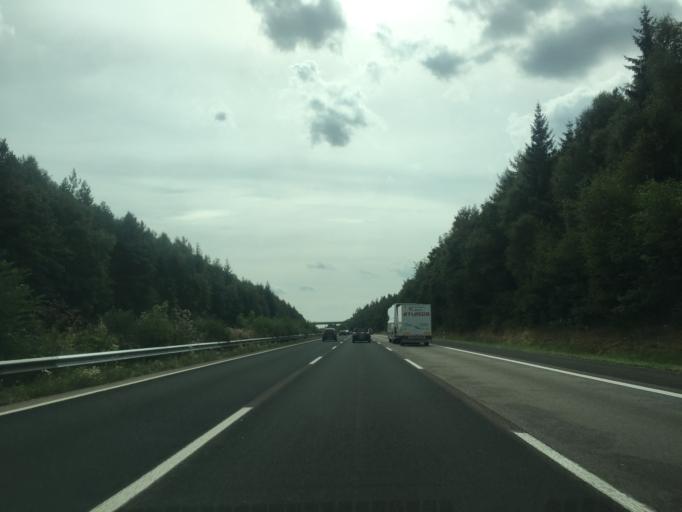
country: DE
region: Rheinland-Pfalz
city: Birkheim
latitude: 50.1032
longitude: 7.6035
